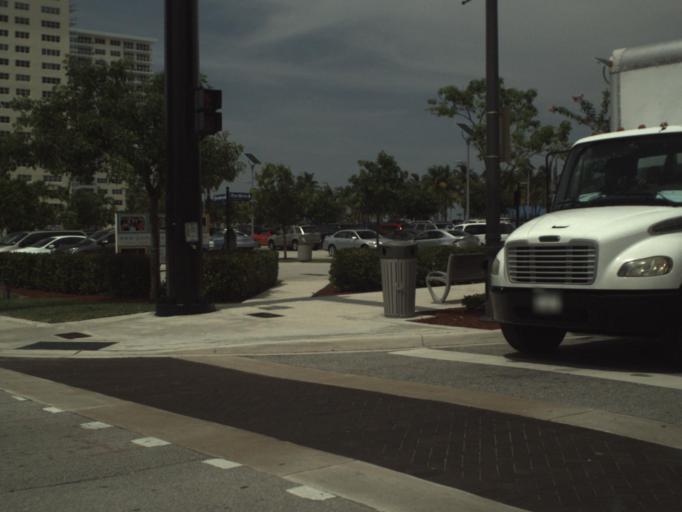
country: US
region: Florida
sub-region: Broward County
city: Terra Mar
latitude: 26.2319
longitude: -80.0908
